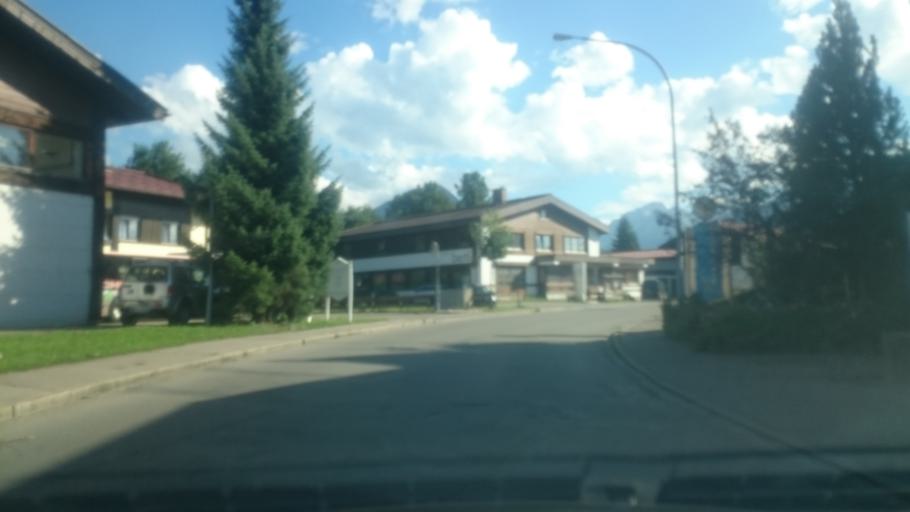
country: DE
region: Bavaria
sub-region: Swabia
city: Oberstdorf
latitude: 47.4158
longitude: 10.2827
